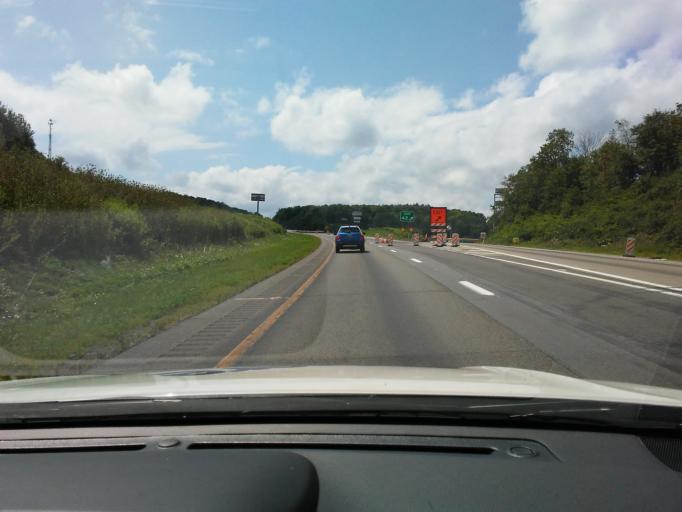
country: US
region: Pennsylvania
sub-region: Venango County
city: Seneca
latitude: 41.1741
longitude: -79.7352
